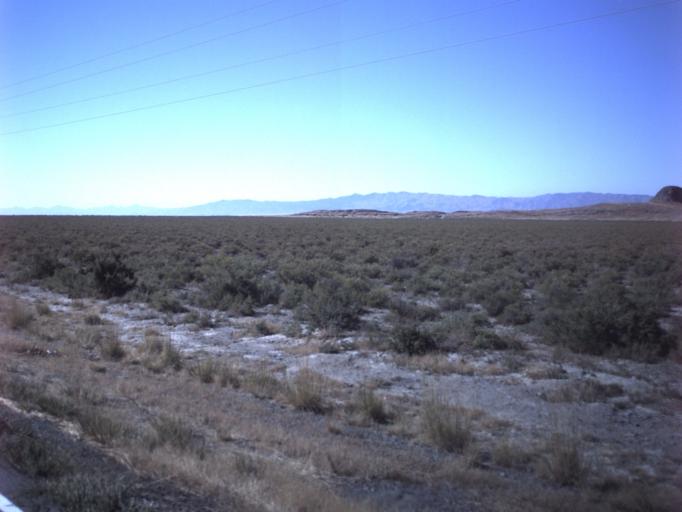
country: US
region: Utah
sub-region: Tooele County
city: Grantsville
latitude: 40.7155
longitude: -112.6616
